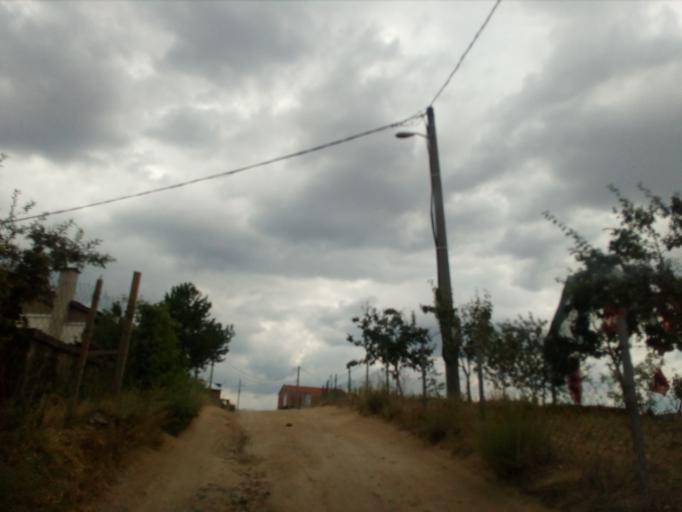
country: MK
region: Veles
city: Veles
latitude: 41.7090
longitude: 21.7586
